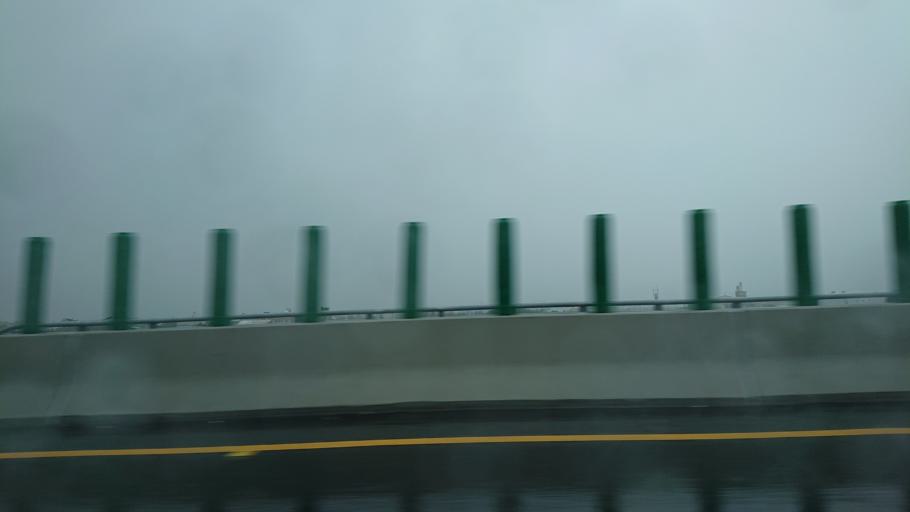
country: TW
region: Taiwan
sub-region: Changhua
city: Chang-hua
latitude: 23.9387
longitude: 120.3219
